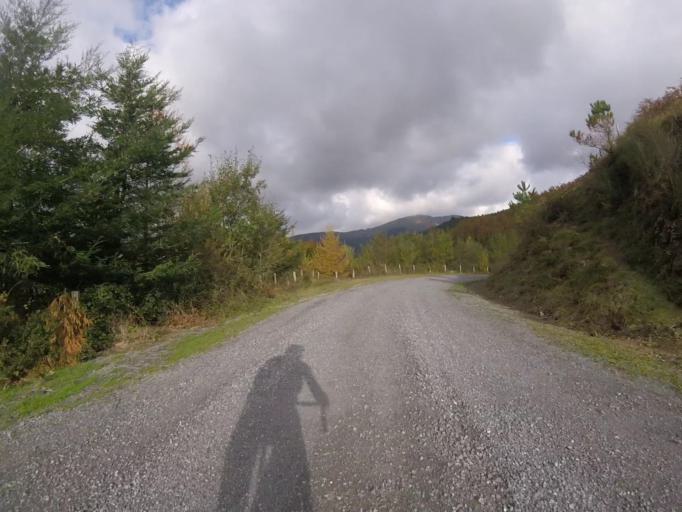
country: ES
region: Navarre
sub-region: Provincia de Navarra
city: Goizueta
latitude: 43.2136
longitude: -1.8326
